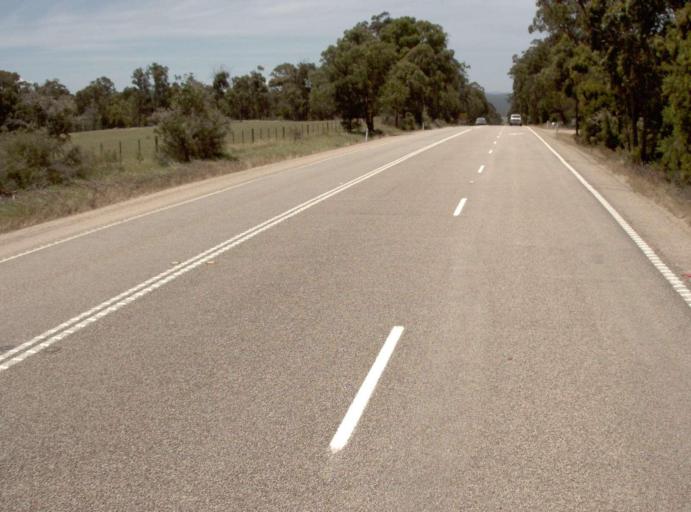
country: AU
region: Victoria
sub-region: East Gippsland
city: Bairnsdale
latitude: -37.7765
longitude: 147.6865
